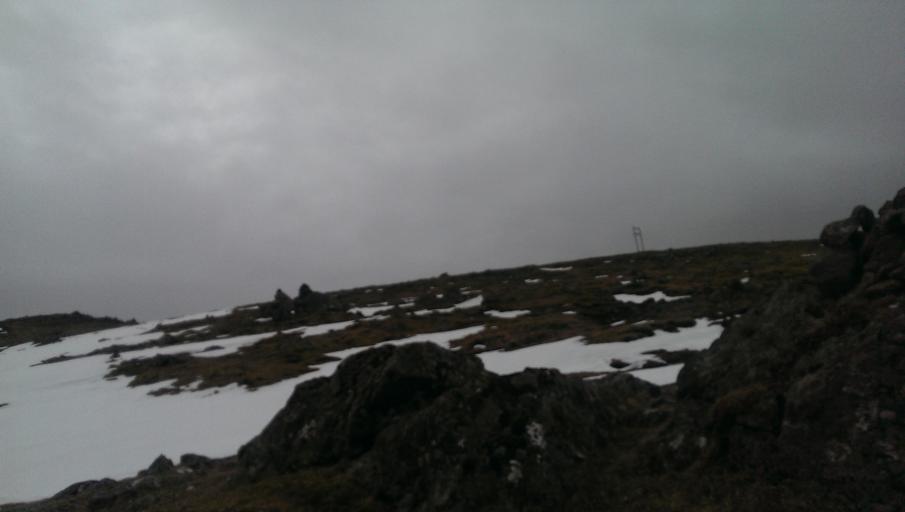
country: FO
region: Streymoy
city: Kollafjordhur
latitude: 62.0307
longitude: -6.8832
